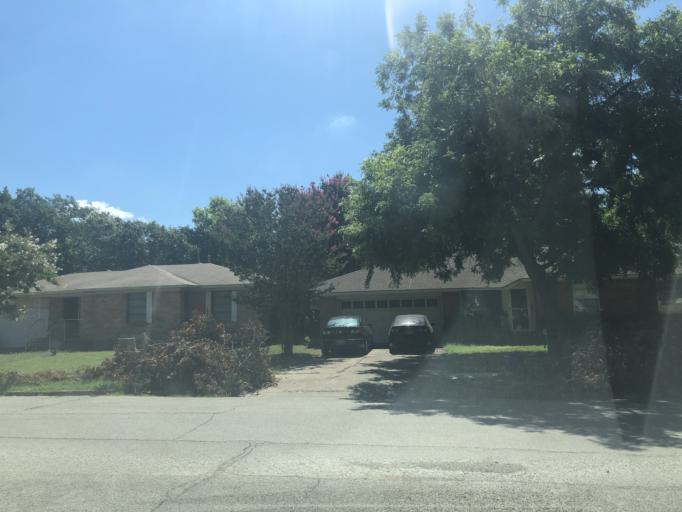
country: US
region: Texas
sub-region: Dallas County
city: Duncanville
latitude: 32.6526
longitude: -96.9103
